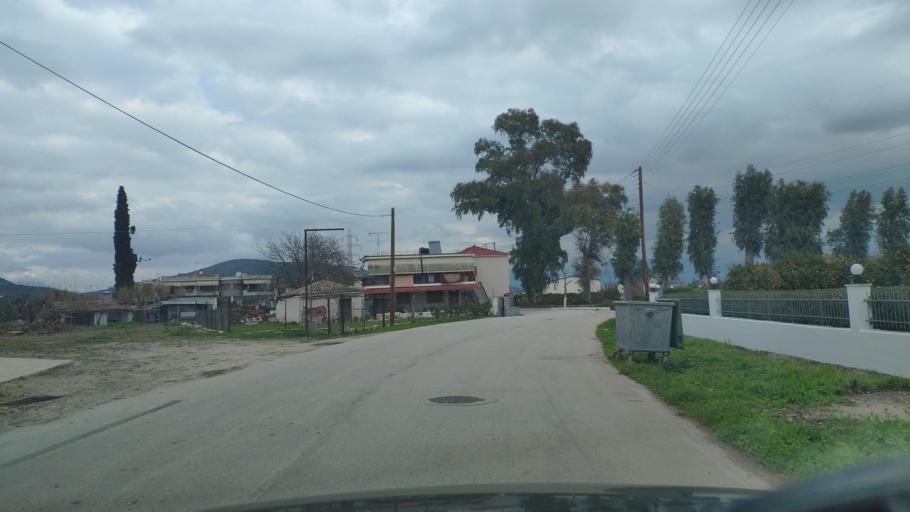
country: GR
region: Peloponnese
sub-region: Nomos Argolidos
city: Nea Kios
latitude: 37.5966
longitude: 22.7021
